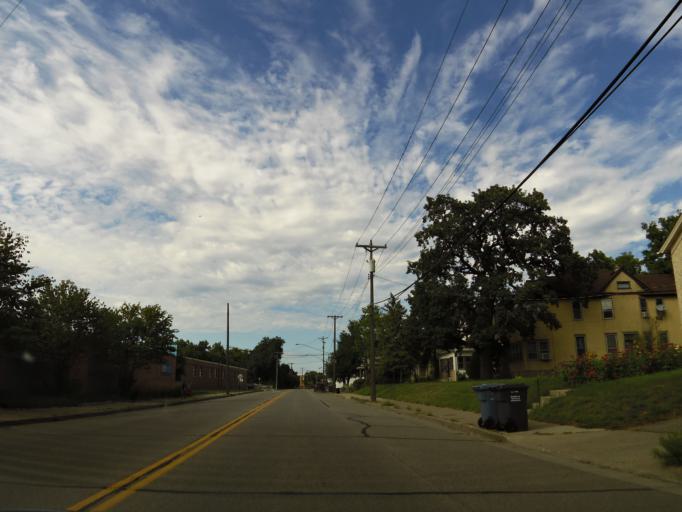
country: US
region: Minnesota
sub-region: Hennepin County
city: Minneapolis
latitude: 45.0047
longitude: -93.2714
